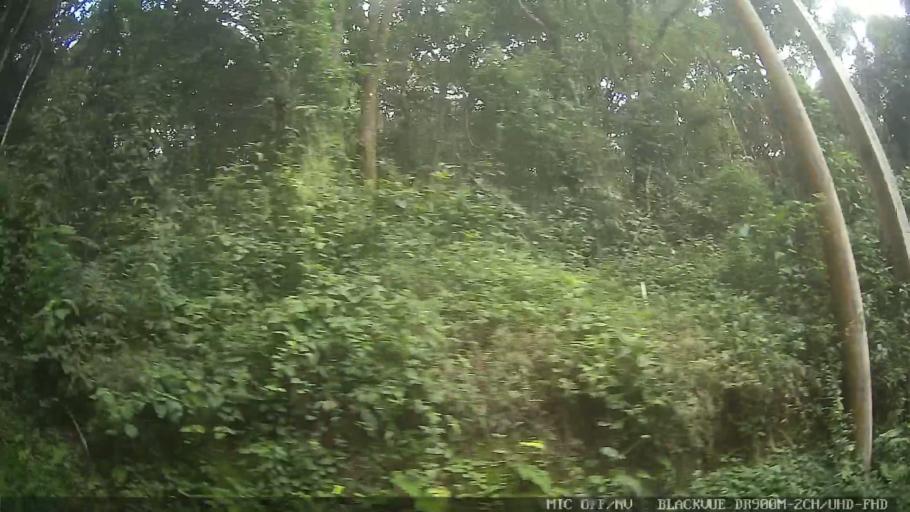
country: BR
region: Minas Gerais
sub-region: Extrema
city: Extrema
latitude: -22.8833
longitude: -46.3133
